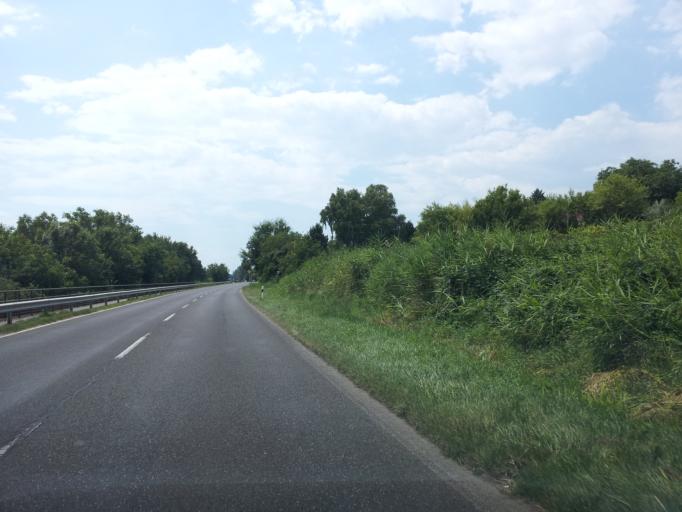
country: HU
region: Veszprem
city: Balatonalmadi
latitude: 47.0009
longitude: 17.9989
